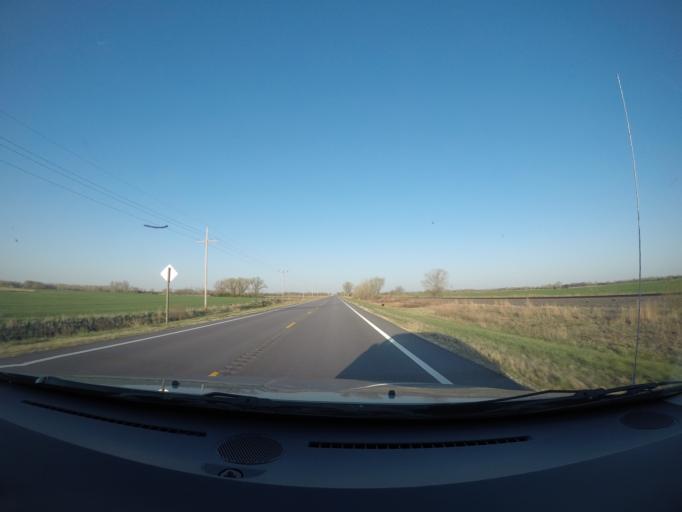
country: US
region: Kansas
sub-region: Stafford County
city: Stafford
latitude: 37.8373
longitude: -98.3643
